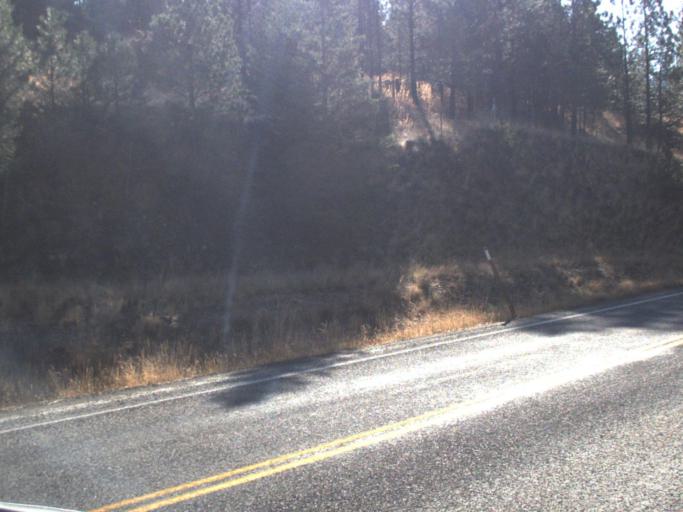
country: US
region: Washington
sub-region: Ferry County
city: Republic
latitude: 48.6584
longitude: -118.6684
